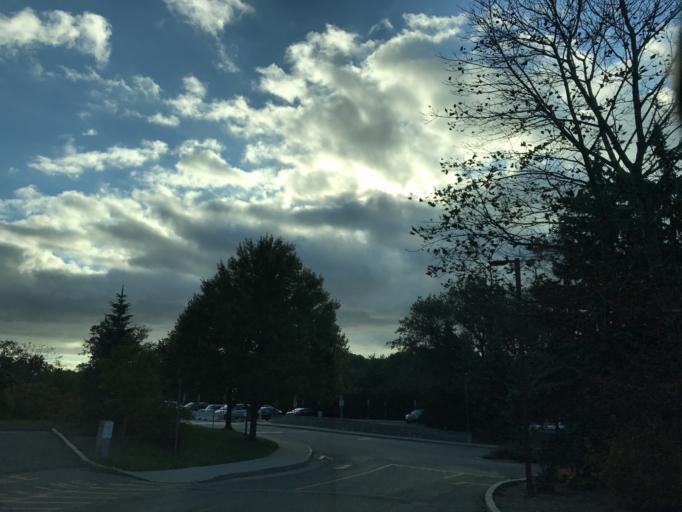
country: US
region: Massachusetts
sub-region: Suffolk County
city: Jamaica Plain
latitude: 42.3009
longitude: -71.1292
